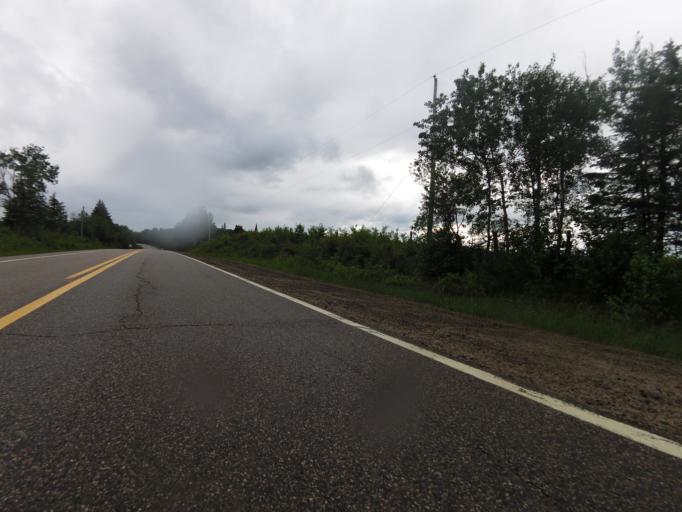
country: CA
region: Quebec
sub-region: Outaouais
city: Shawville
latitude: 45.9272
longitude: -76.2354
